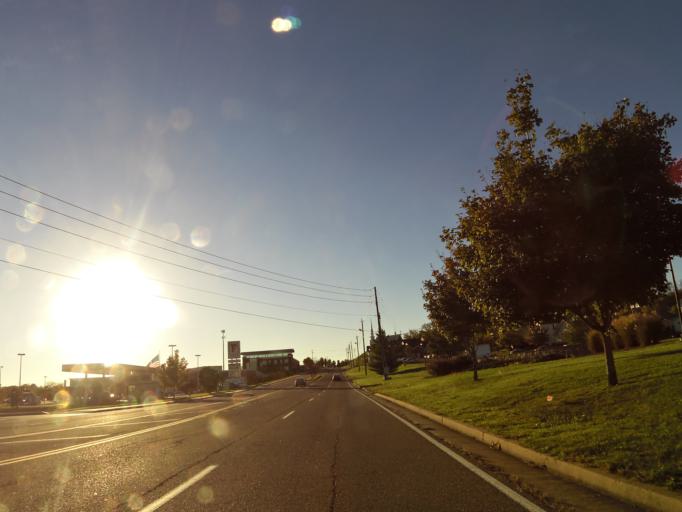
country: US
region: Tennessee
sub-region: Knox County
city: Knoxville
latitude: 35.9668
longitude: -83.9414
